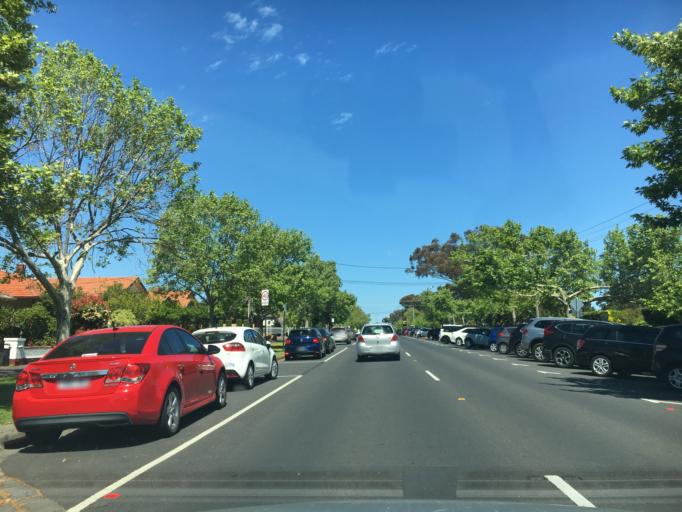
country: AU
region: Victoria
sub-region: Monash
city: Chadstone
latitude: -37.8948
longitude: 145.0905
